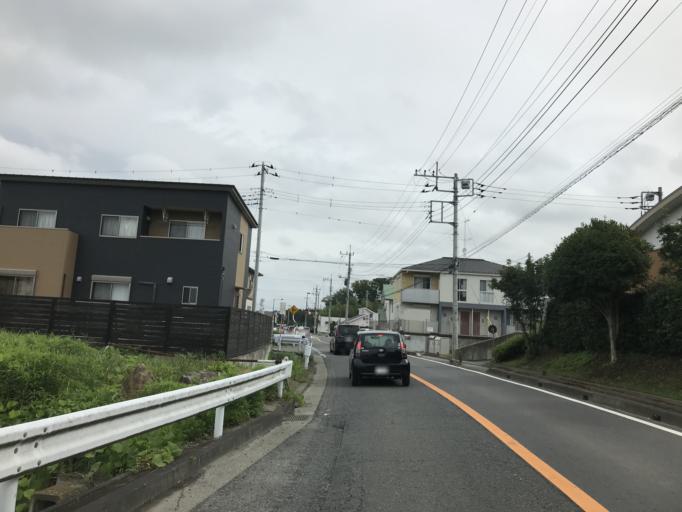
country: JP
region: Ibaraki
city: Mito-shi
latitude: 36.3354
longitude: 140.4587
